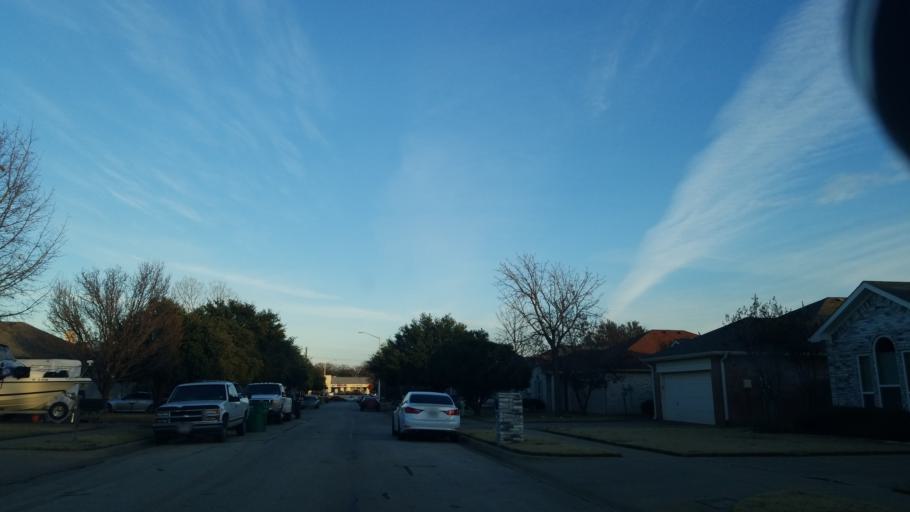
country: US
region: Texas
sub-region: Denton County
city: Corinth
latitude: 33.1588
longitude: -97.1079
